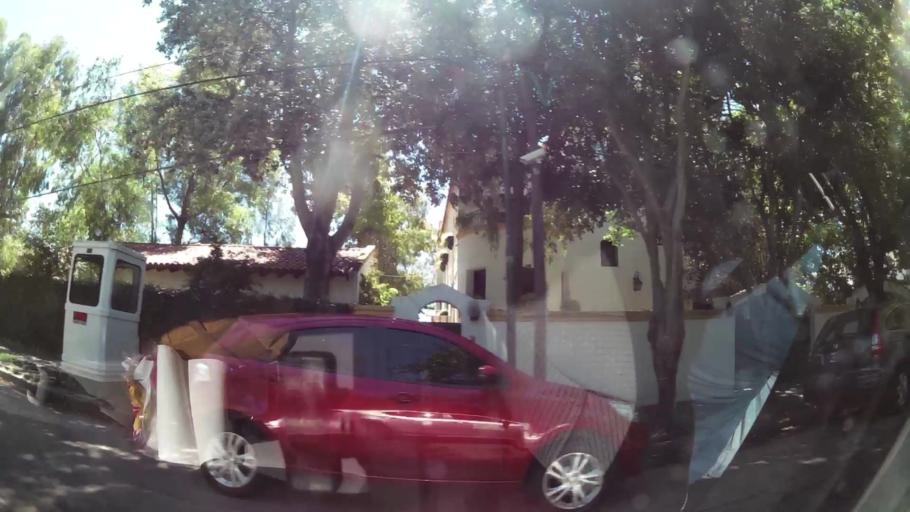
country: AR
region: Buenos Aires
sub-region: Partido de San Isidro
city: San Isidro
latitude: -34.4549
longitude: -58.5149
